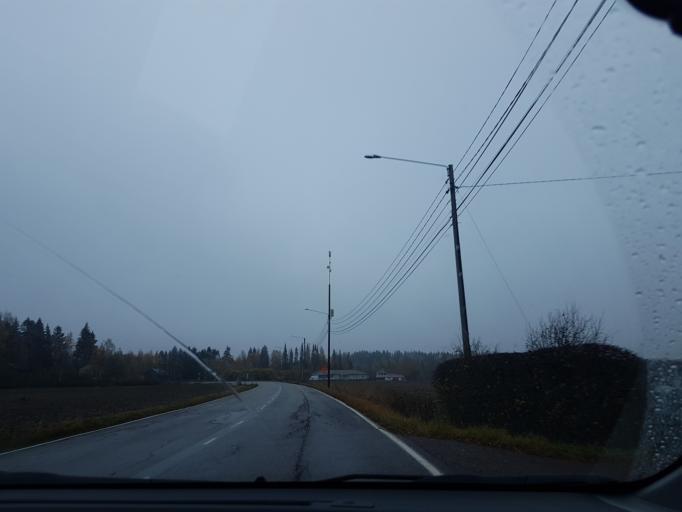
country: FI
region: Uusimaa
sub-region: Helsinki
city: Maentsaelae
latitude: 60.6158
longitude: 25.2392
